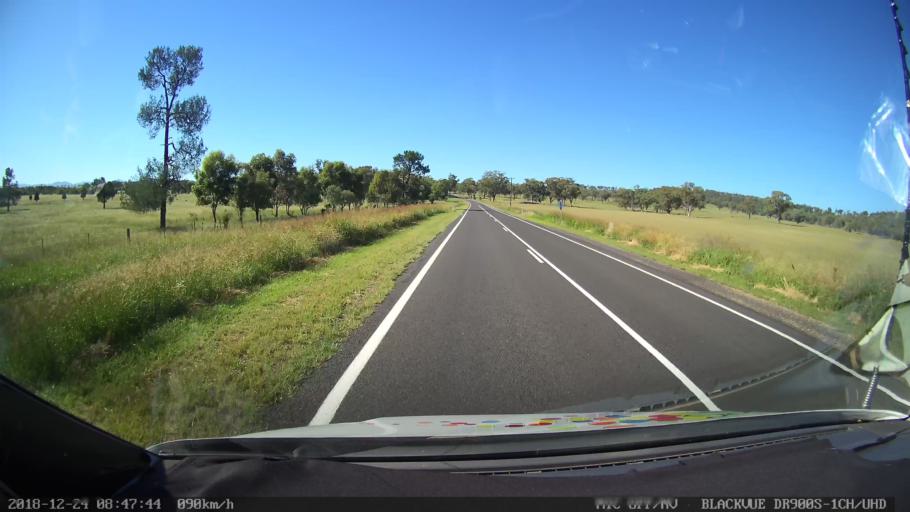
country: AU
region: New South Wales
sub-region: Liverpool Plains
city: Quirindi
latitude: -31.4462
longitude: 150.6468
